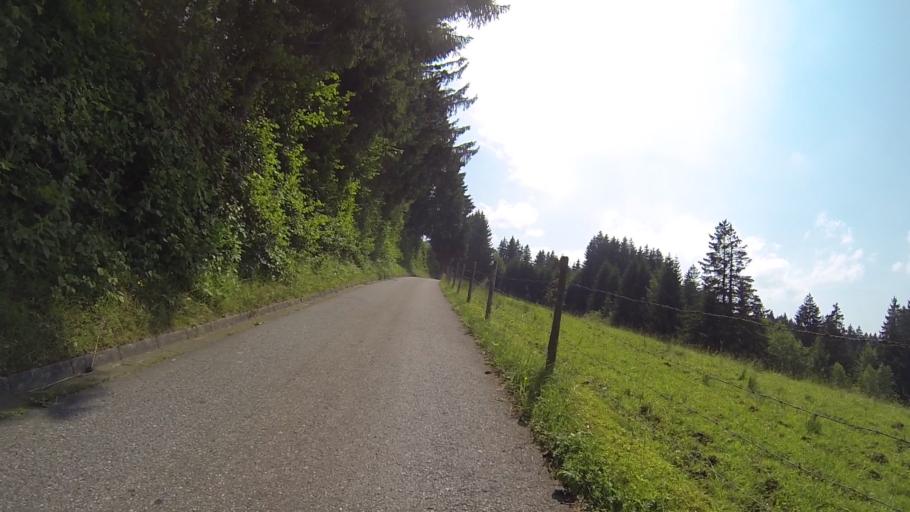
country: DE
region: Bavaria
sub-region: Swabia
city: Nesselwang
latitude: 47.6137
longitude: 10.4765
